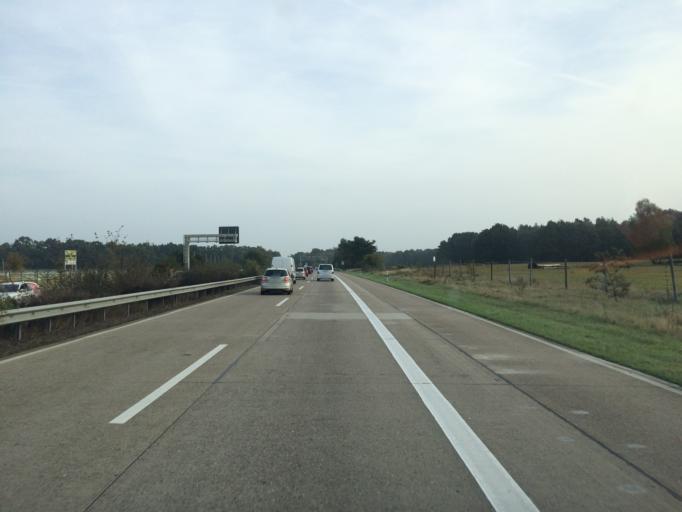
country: DE
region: Lower Saxony
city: Bad Fallingbostel
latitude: 52.8968
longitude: 9.7782
